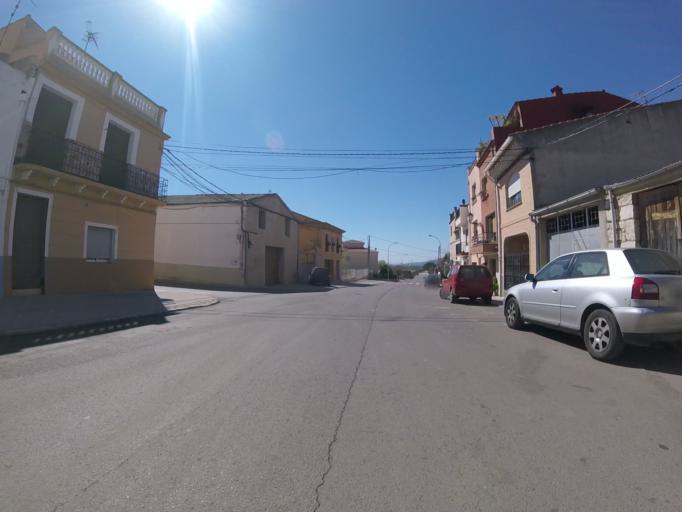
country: ES
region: Valencia
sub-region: Provincia de Castello
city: Chert/Xert
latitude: 40.4167
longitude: 0.1735
